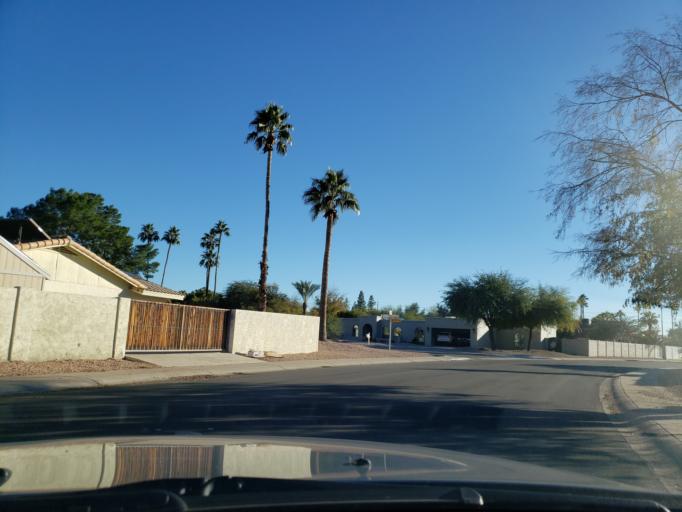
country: US
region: Arizona
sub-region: Maricopa County
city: Paradise Valley
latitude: 33.5994
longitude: -111.9702
